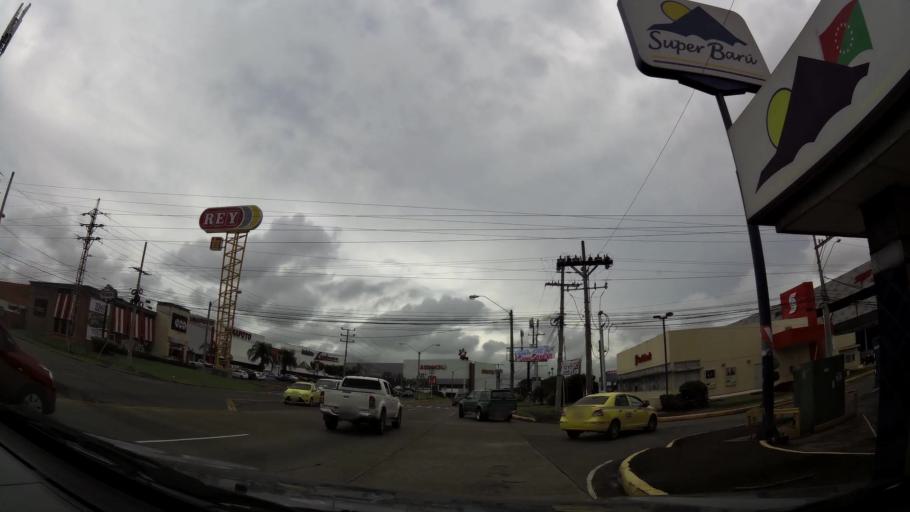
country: PA
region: Chiriqui
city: David
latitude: 8.4452
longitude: -82.4216
